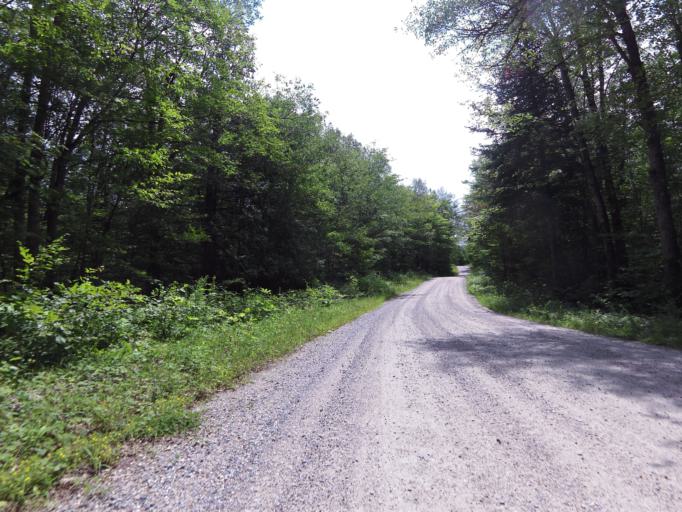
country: CA
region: Ontario
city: Perth
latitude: 44.7789
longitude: -76.6089
